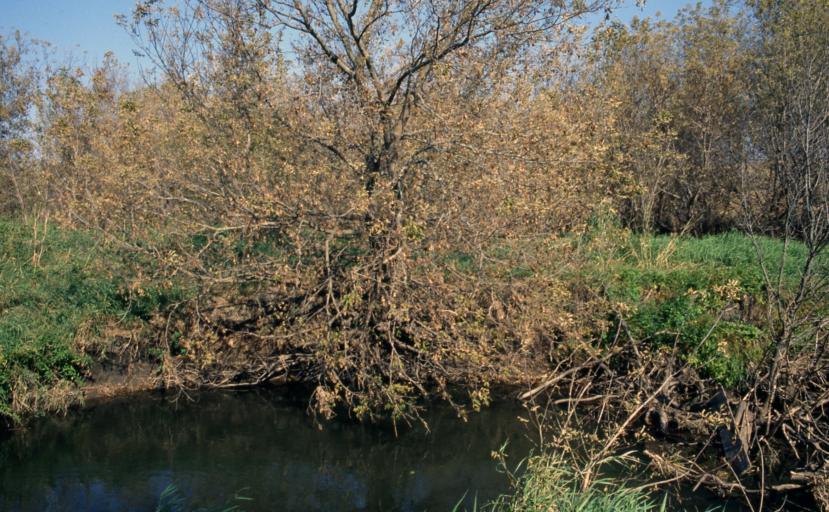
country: US
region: Minnesota
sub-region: Wabasha County
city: Elgin
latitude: 44.1204
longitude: -92.2245
